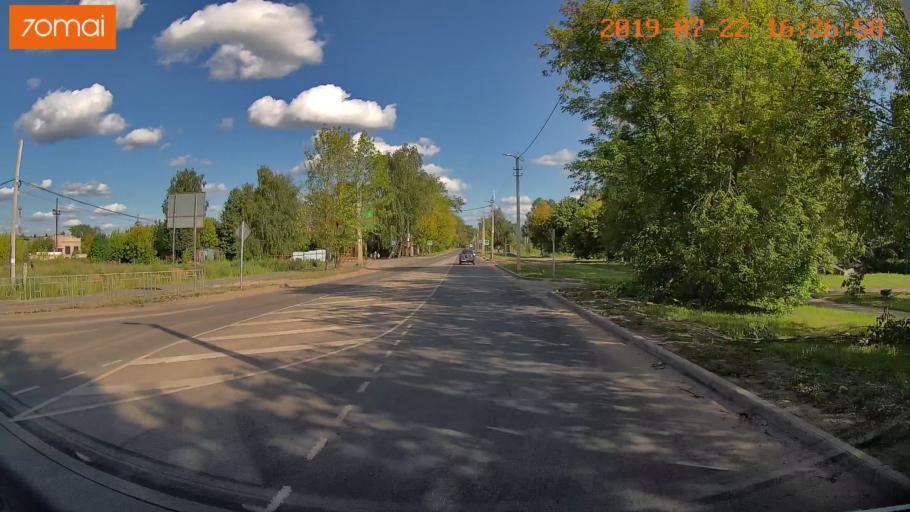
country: RU
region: Ivanovo
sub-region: Gorod Ivanovo
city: Ivanovo
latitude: 57.0463
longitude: 40.9405
